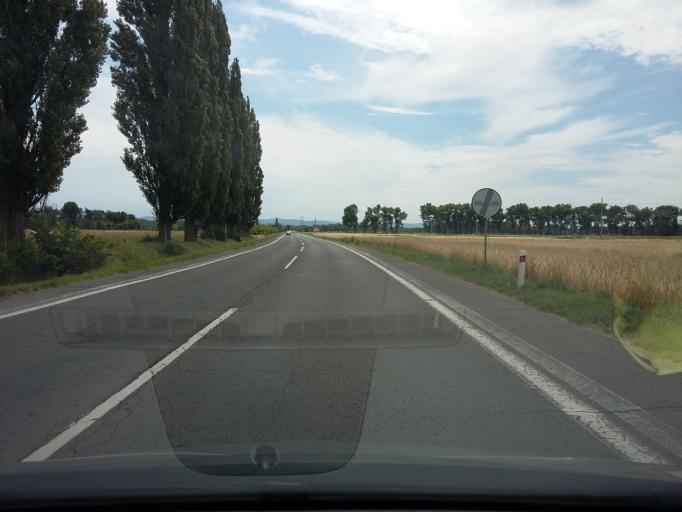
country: SK
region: Bratislavsky
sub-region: Okres Malacky
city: Malacky
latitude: 48.4966
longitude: 17.0042
